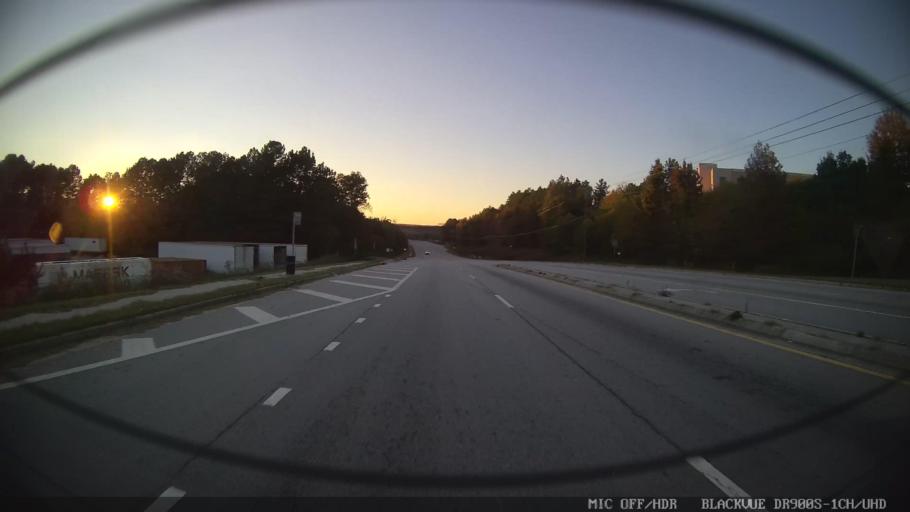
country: US
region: Georgia
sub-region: Clayton County
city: Forest Park
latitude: 33.6162
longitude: -84.4058
